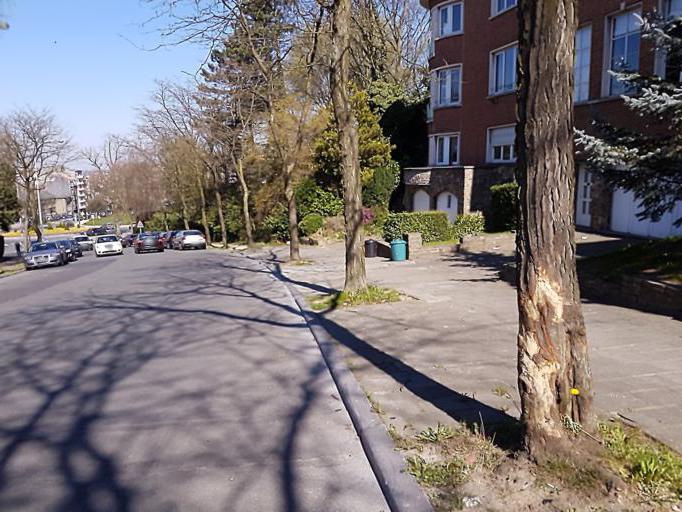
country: BE
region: Brussels Capital
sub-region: Bruxelles-Capitale
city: Brussels
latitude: 50.8199
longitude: 4.3346
